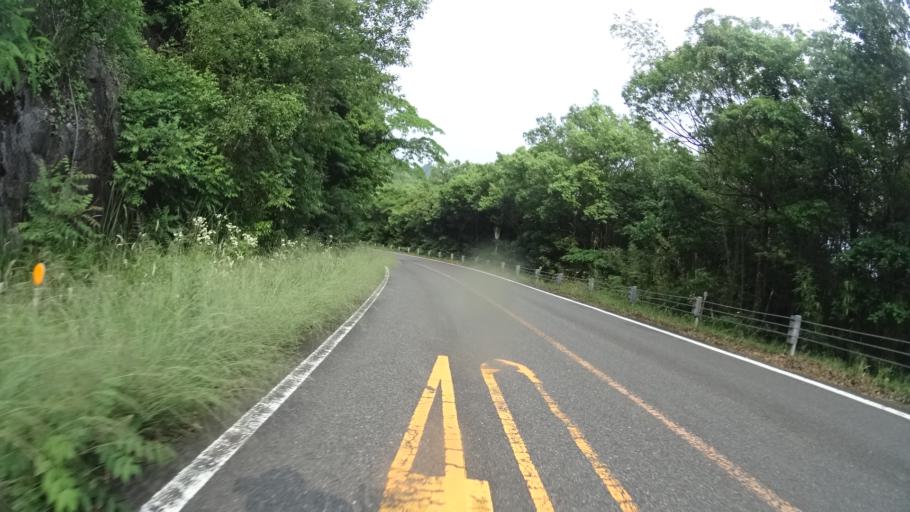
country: JP
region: Yamaguchi
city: Ogori-shimogo
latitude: 34.2277
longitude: 131.3063
